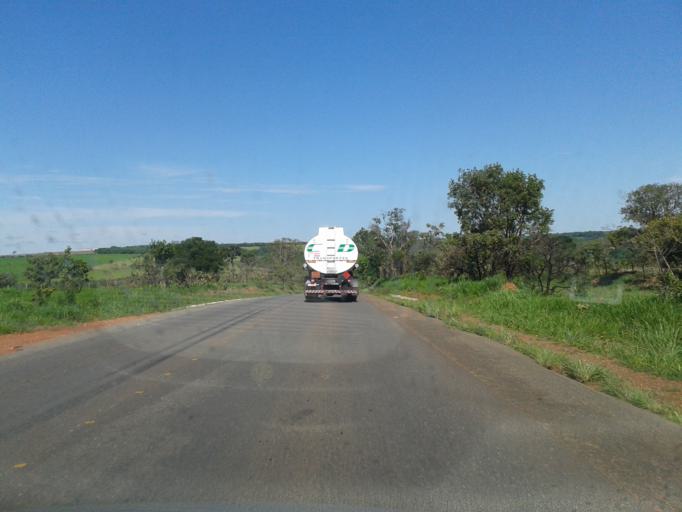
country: BR
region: Goias
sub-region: Bela Vista De Goias
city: Bela Vista de Goias
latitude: -17.0535
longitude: -48.9308
